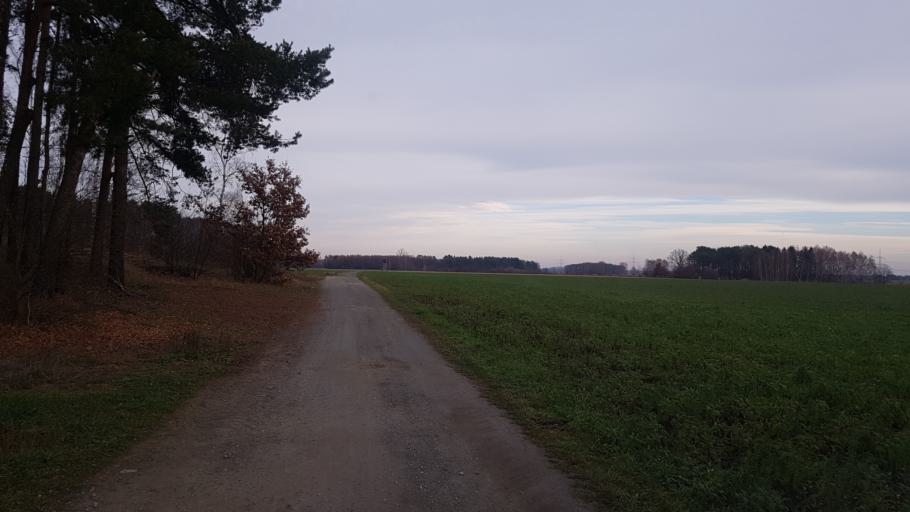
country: DE
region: Brandenburg
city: Schonborn
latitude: 51.5657
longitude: 13.4868
